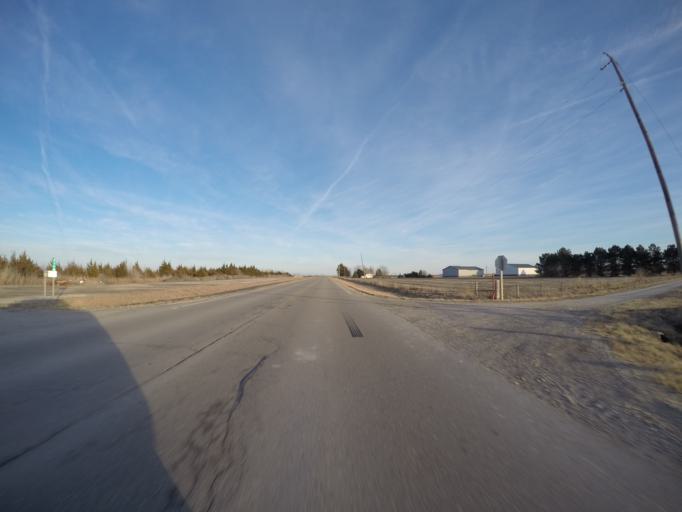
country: US
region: Kansas
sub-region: Dickinson County
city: Herington
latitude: 38.6643
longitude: -96.8751
